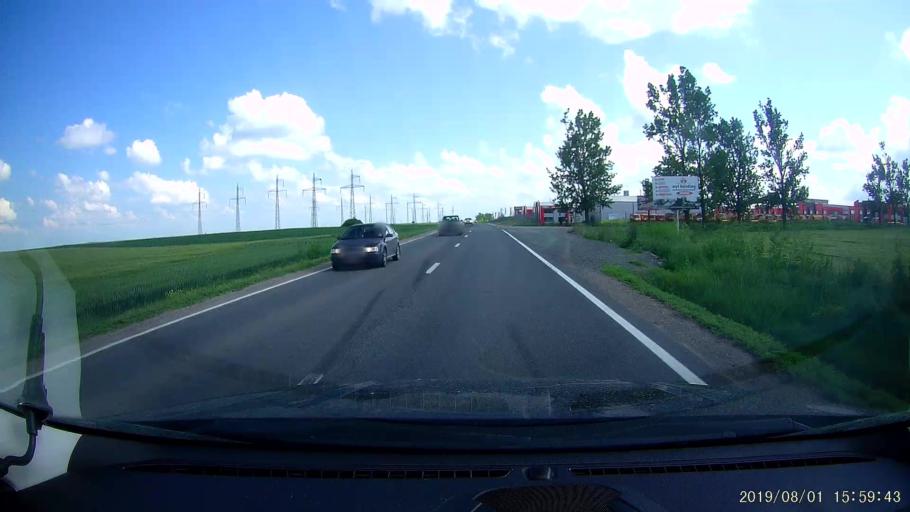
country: RO
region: Ialomita
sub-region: Comuna Slobozia
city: Slobozia
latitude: 44.5426
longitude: 27.3852
